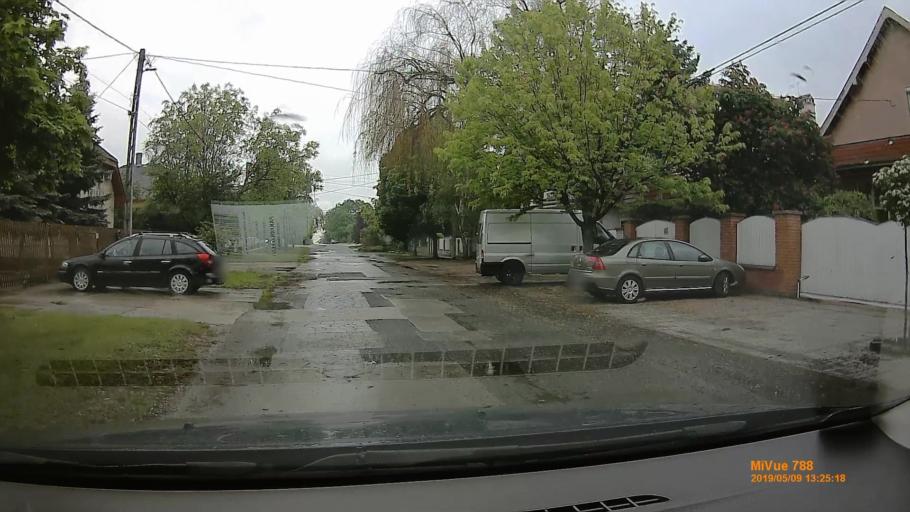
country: HU
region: Budapest
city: Budapest XVI. keruelet
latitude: 47.5382
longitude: 19.1886
